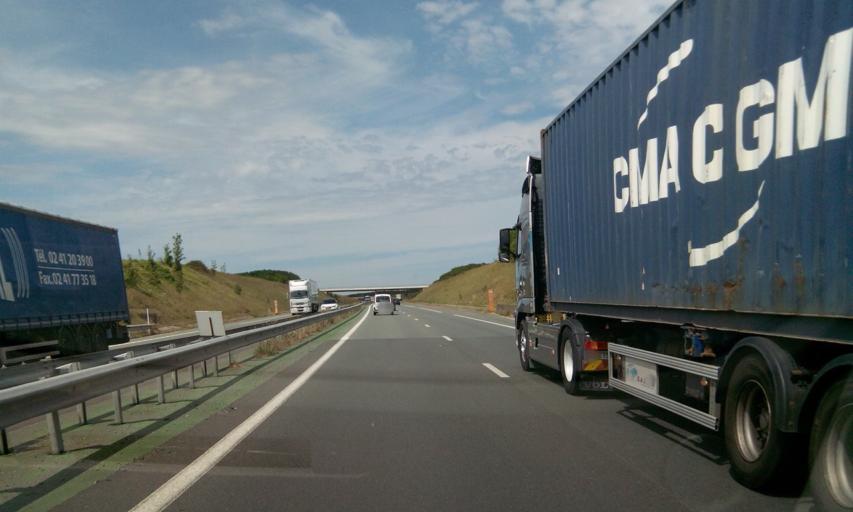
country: FR
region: Poitou-Charentes
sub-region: Departement des Deux-Sevres
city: Saint-Gelais
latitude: 46.3843
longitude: -0.3670
